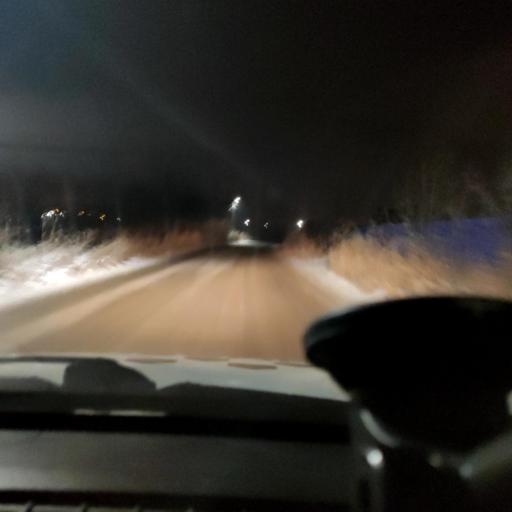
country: RU
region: Perm
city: Ferma
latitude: 57.8960
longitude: 56.2977
